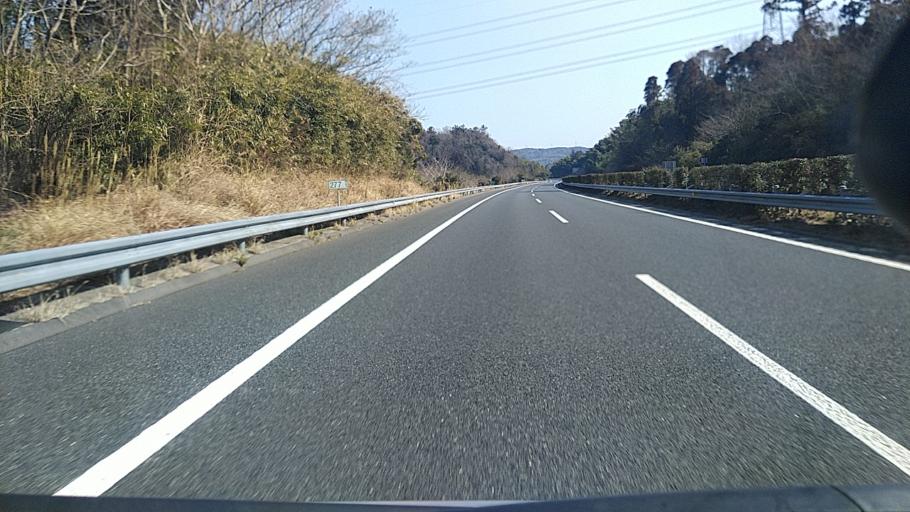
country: JP
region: Chiba
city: Kisarazu
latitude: 35.3579
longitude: 140.0285
